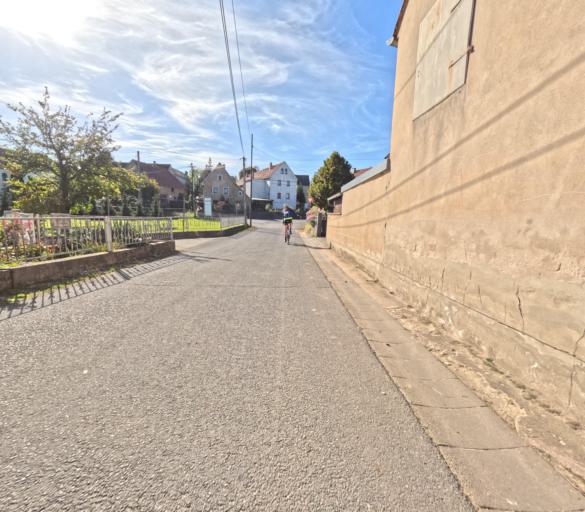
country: DE
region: Saxony
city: Ottendorf-Okrilla
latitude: 51.1634
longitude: 13.7700
